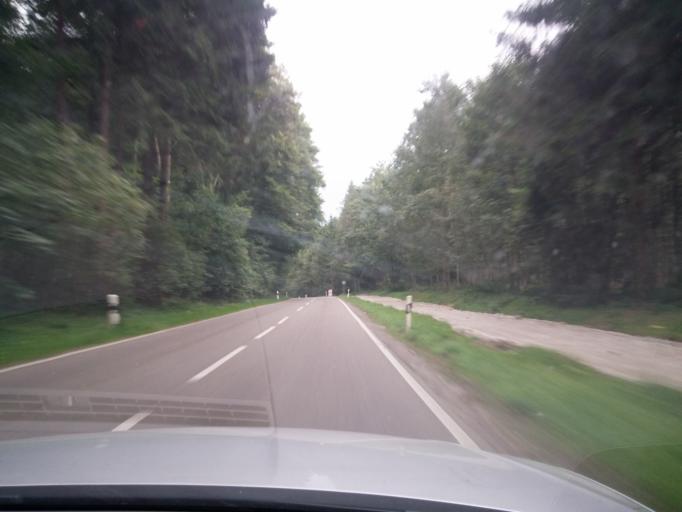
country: DE
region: Bavaria
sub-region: Swabia
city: Memmingen
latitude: 47.9551
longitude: 10.1802
